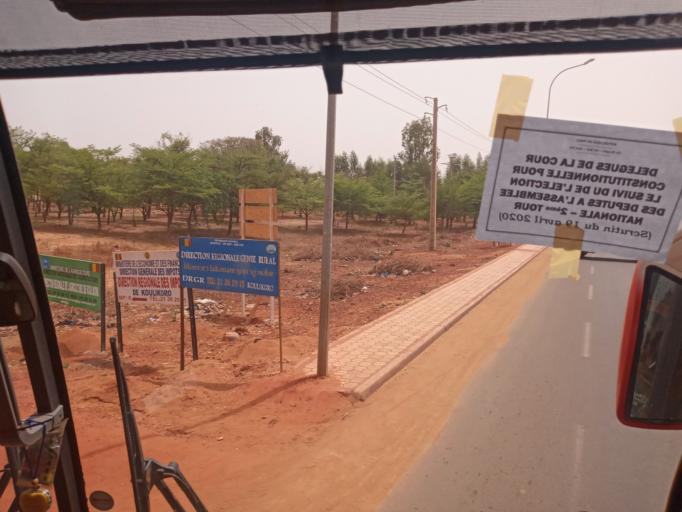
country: ML
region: Koulikoro
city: Koulikoro
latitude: 12.8437
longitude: -7.5841
